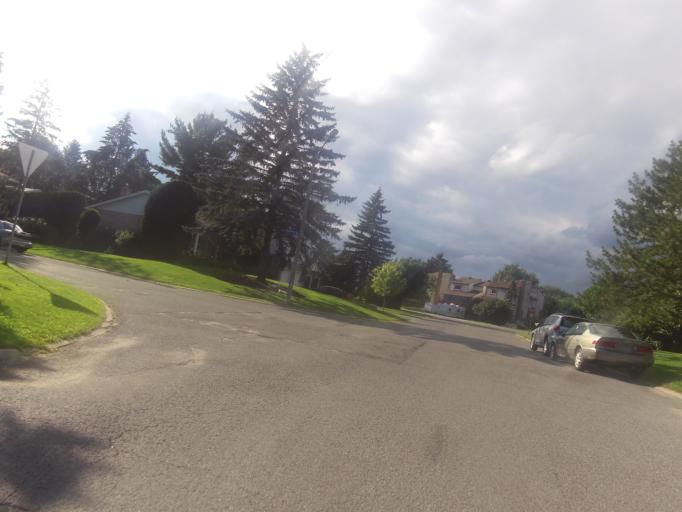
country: CA
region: Ontario
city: Bells Corners
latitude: 45.3318
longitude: -75.7874
